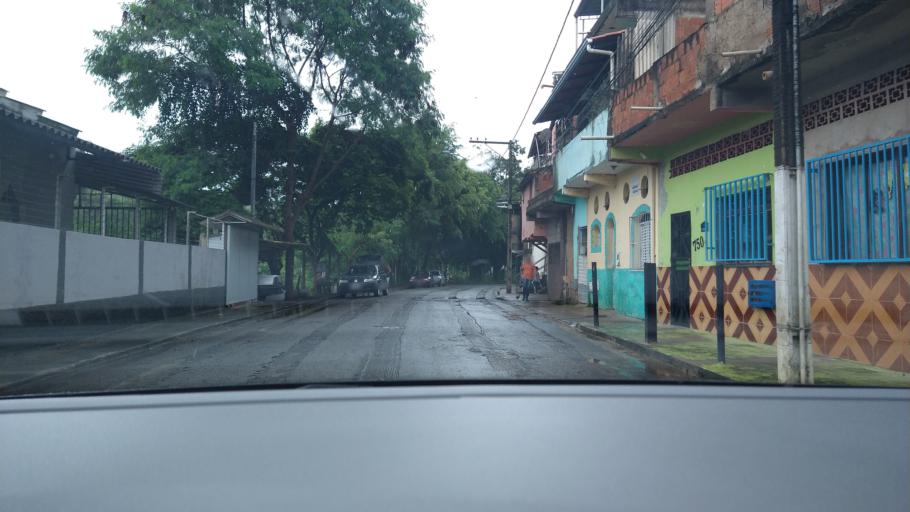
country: BR
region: Minas Gerais
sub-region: Ponte Nova
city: Ponte Nova
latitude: -20.4016
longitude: -42.9008
